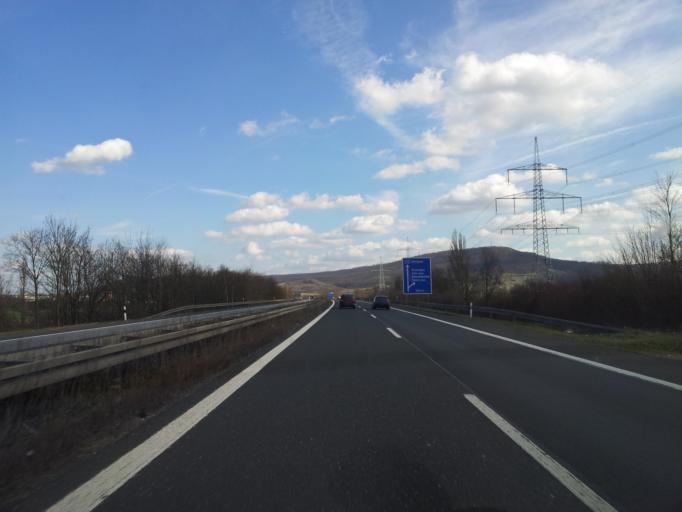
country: DE
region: Bavaria
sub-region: Regierungsbezirk Unterfranken
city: Knetzgau
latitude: 49.9821
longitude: 10.5450
